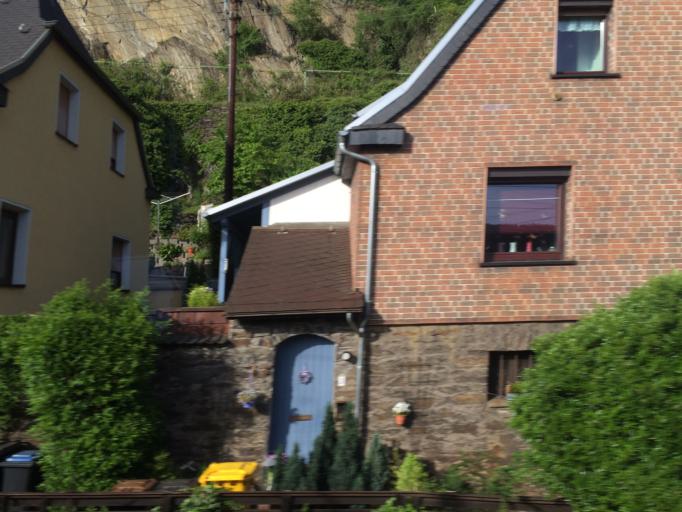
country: DE
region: Rheinland-Pfalz
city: Sankt Goarshausen
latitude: 50.1502
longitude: 7.7254
